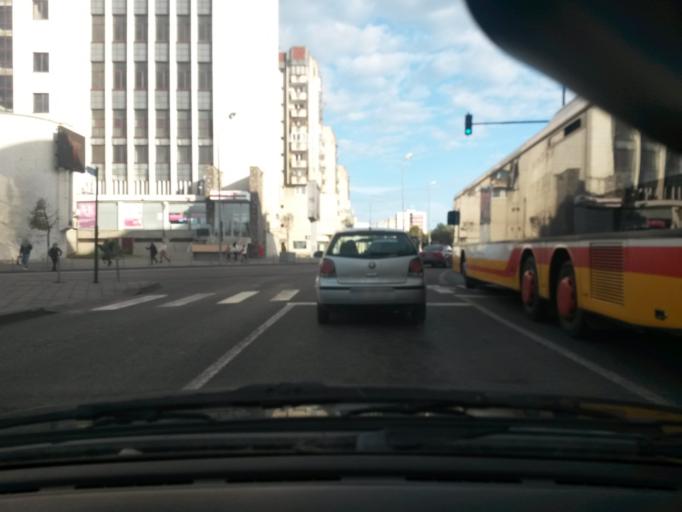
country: RO
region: Mures
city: Targu-Mures
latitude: 46.5403
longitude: 24.5577
